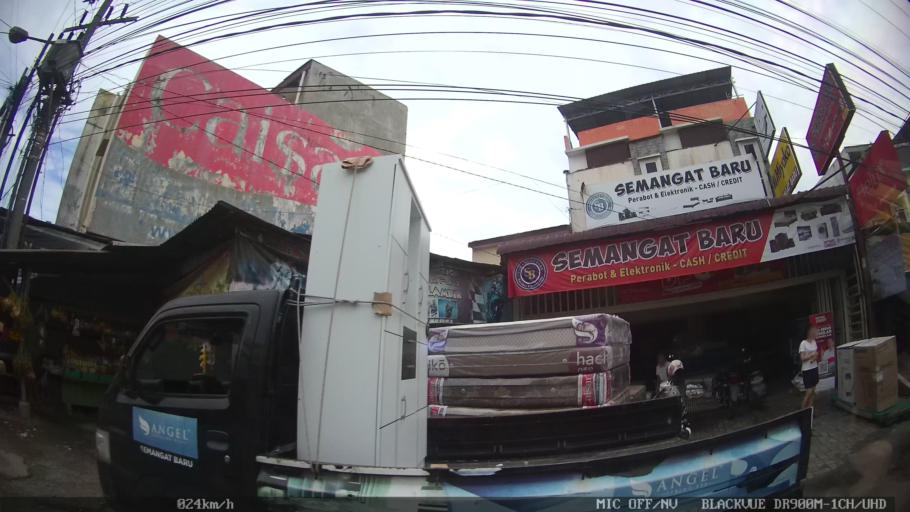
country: ID
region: North Sumatra
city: Sunggal
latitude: 3.6111
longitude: 98.6074
